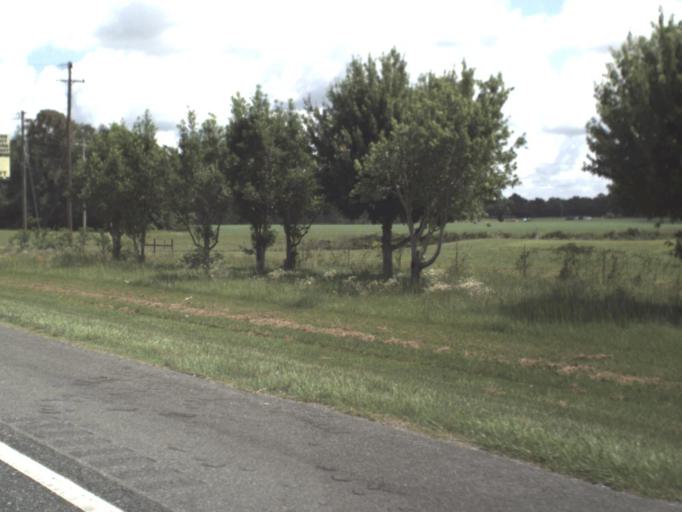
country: US
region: Florida
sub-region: Columbia County
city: Lake City
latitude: 30.1257
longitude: -82.6602
